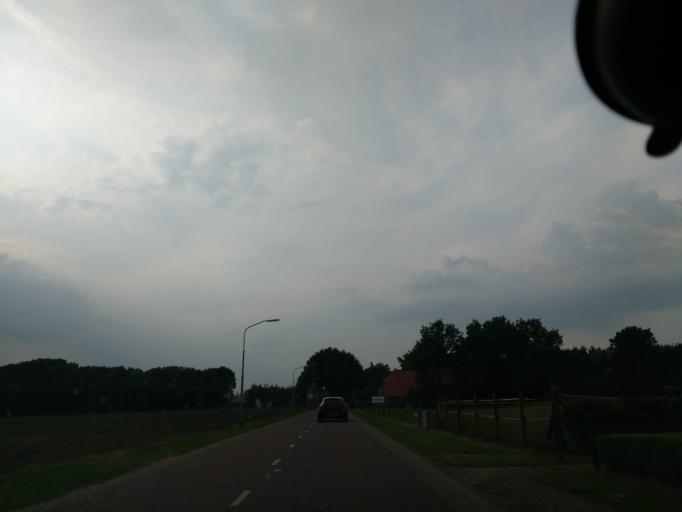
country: NL
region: Drenthe
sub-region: Gemeente Borger-Odoorn
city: Borger
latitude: 52.9018
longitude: 6.8125
